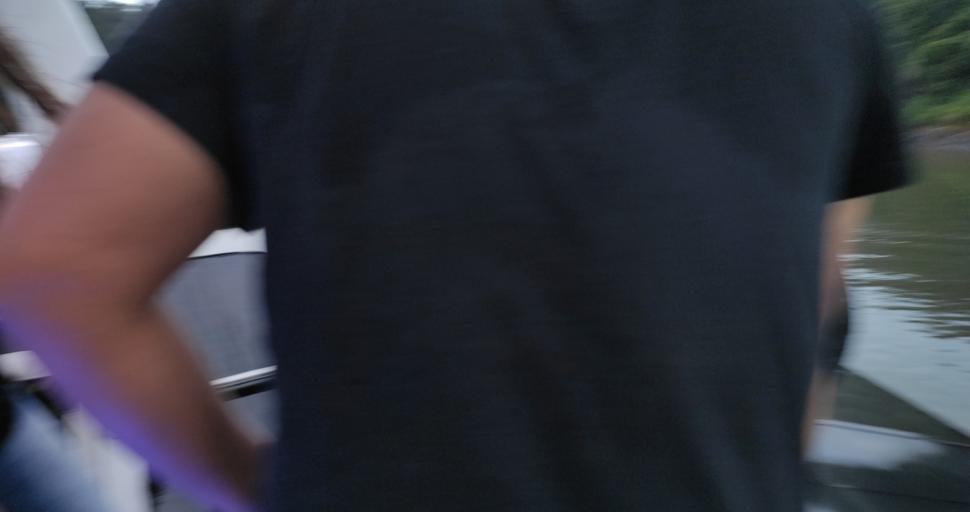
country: AR
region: Misiones
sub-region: Departamento de Iguazu
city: Puerto Iguazu
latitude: -25.5917
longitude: -54.5783
